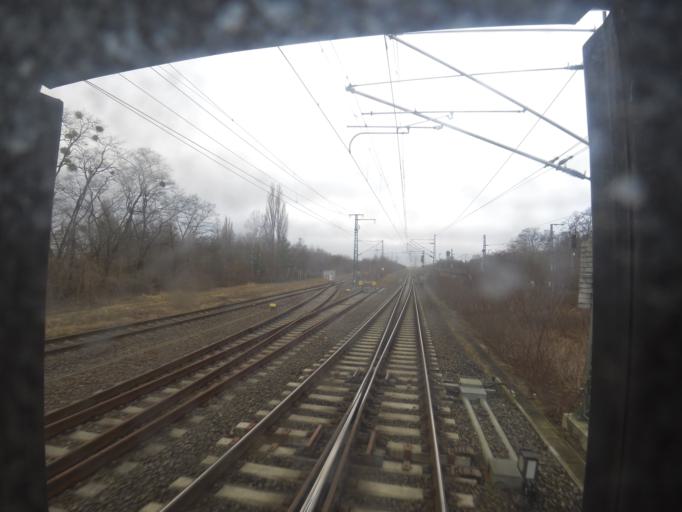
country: DE
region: Berlin
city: Schoneberg Bezirk
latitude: 52.4667
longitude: 13.3621
